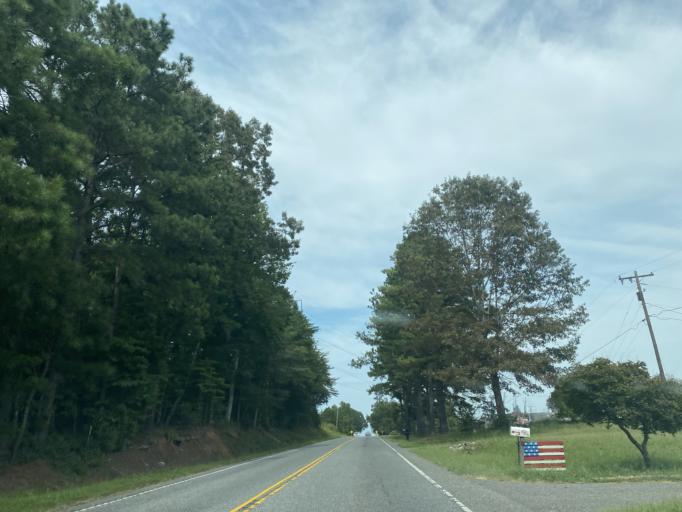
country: US
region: South Carolina
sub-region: Cherokee County
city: Gaffney
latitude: 35.0267
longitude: -81.7103
